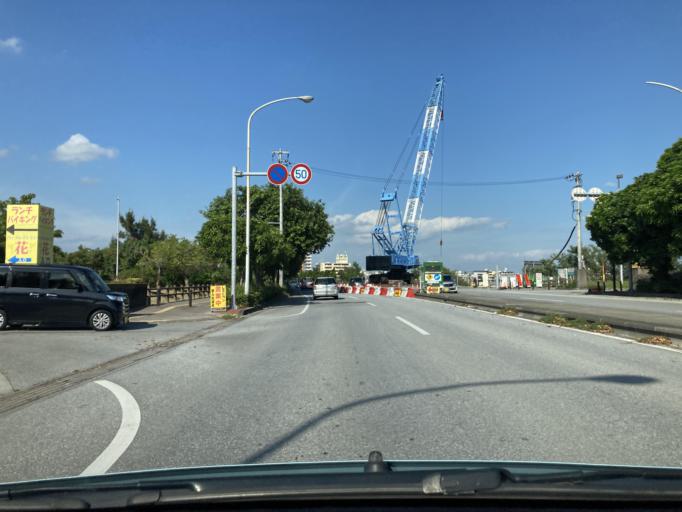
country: JP
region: Okinawa
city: Okinawa
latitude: 26.3098
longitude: 127.8273
